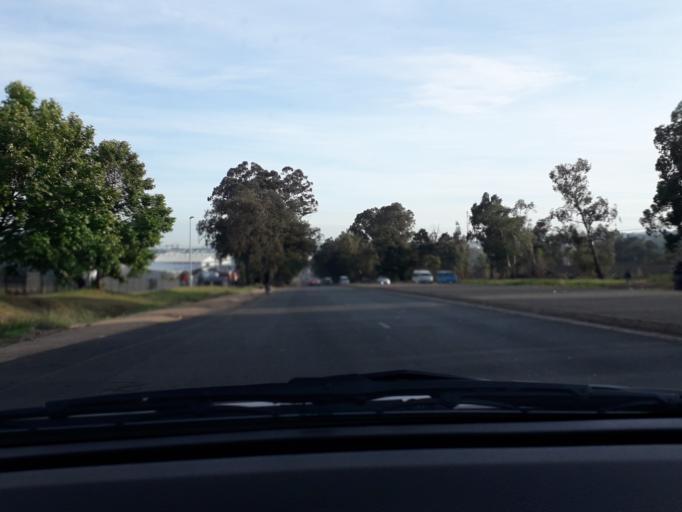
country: ZA
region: Gauteng
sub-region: City of Johannesburg Metropolitan Municipality
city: Midrand
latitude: -25.9367
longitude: 28.1464
